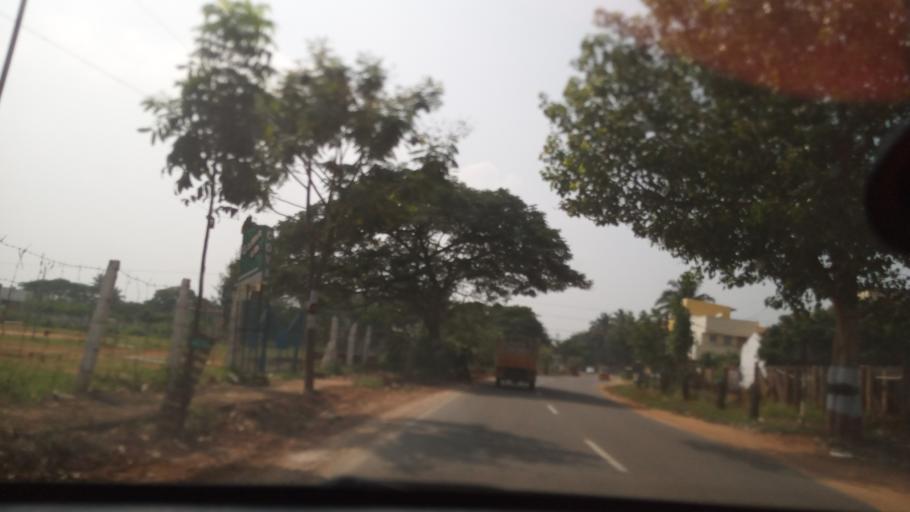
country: IN
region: Tamil Nadu
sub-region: Coimbatore
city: Perur
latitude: 11.0103
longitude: 76.8693
